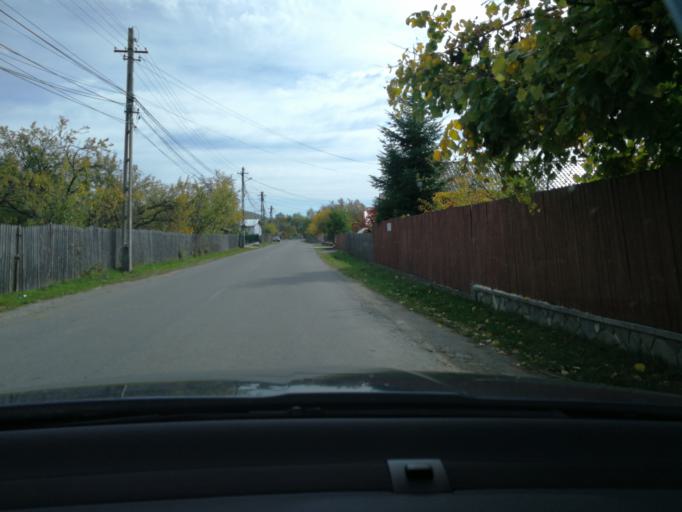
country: RO
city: Brebu Manastirei
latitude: 45.1892
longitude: 25.7648
